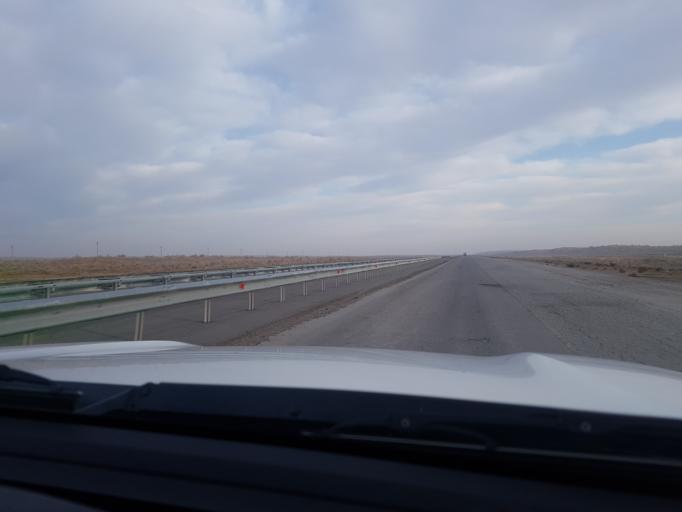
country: TM
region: Ahal
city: Abadan
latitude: 38.5322
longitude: 58.5106
